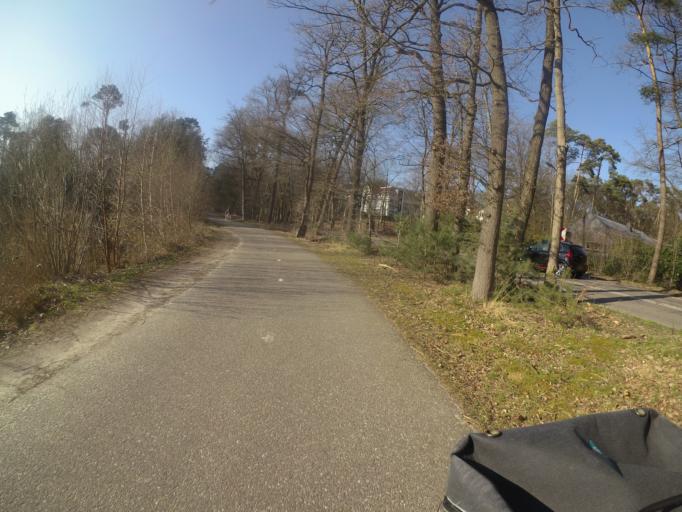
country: NL
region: North Brabant
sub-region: Gemeente Oisterwijk
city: Oisterwijk
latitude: 51.5706
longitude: 5.2156
